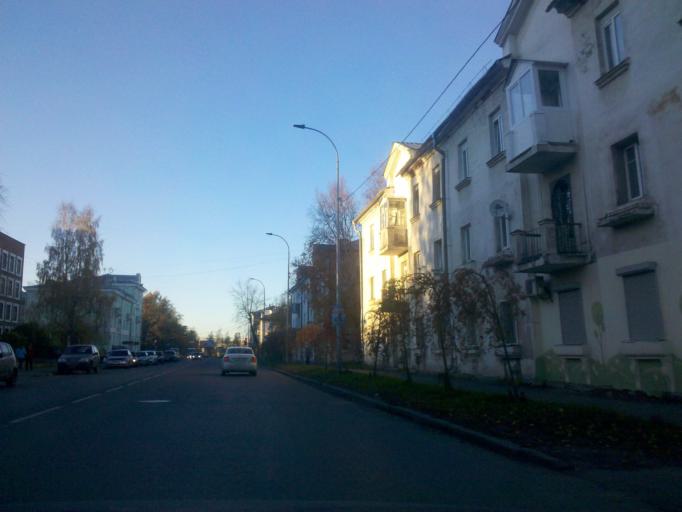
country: RU
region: Republic of Karelia
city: Petrozavodsk
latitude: 61.7807
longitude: 34.3882
